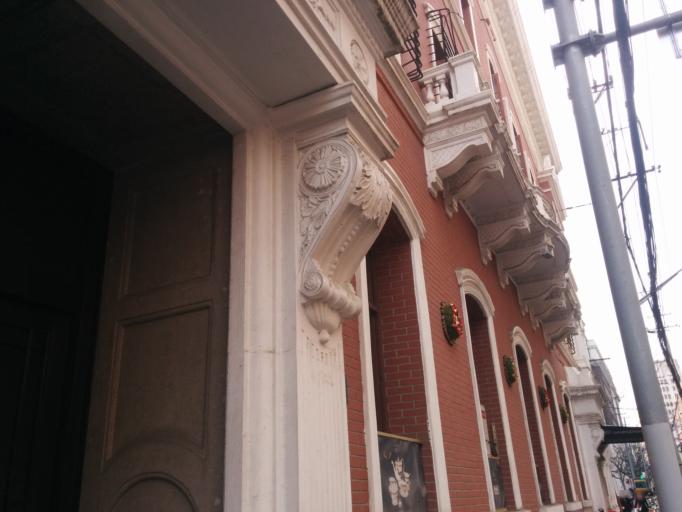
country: CN
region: Shanghai Shi
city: Hongkou
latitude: 31.2374
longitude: 121.4844
